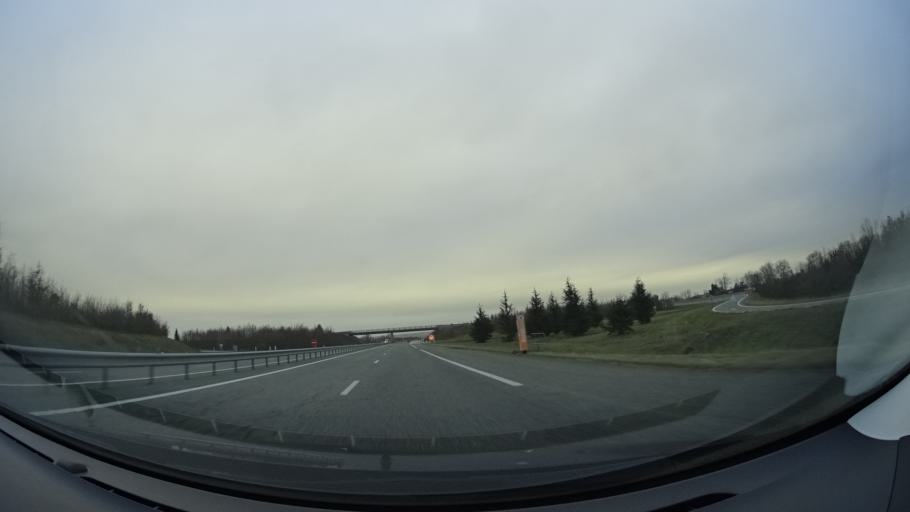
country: FR
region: Midi-Pyrenees
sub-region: Departement de l'Ariege
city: Mazeres
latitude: 43.2333
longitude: 1.6404
